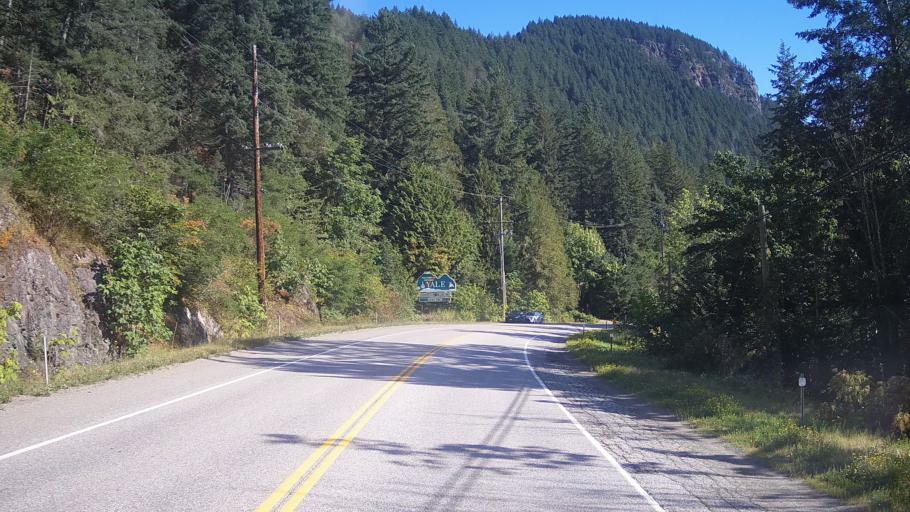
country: CA
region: British Columbia
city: Hope
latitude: 49.5560
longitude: -121.4451
